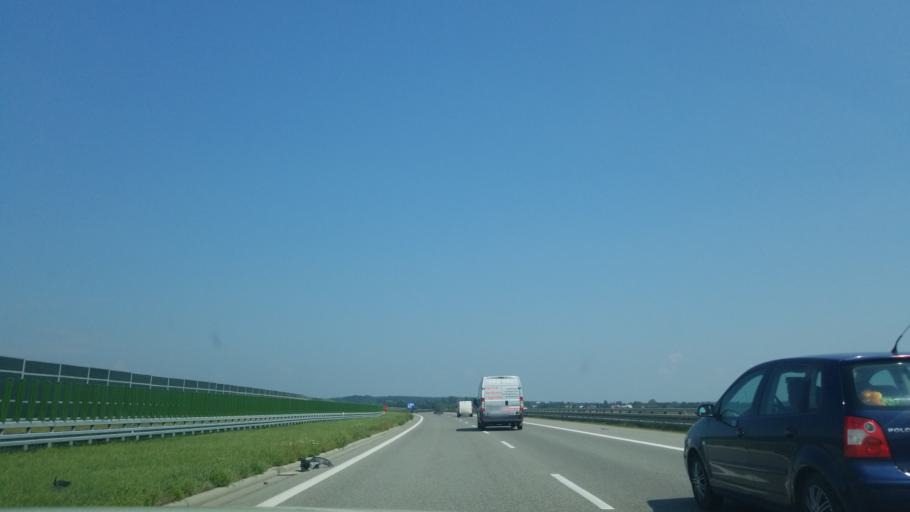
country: PL
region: Subcarpathian Voivodeship
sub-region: Powiat debicki
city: Brzeznica
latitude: 50.0823
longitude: 21.4870
